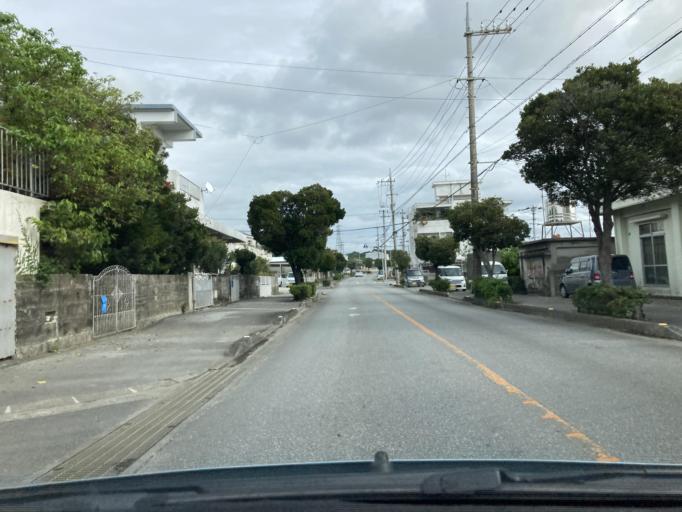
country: JP
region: Okinawa
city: Itoman
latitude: 26.1205
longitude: 127.6823
